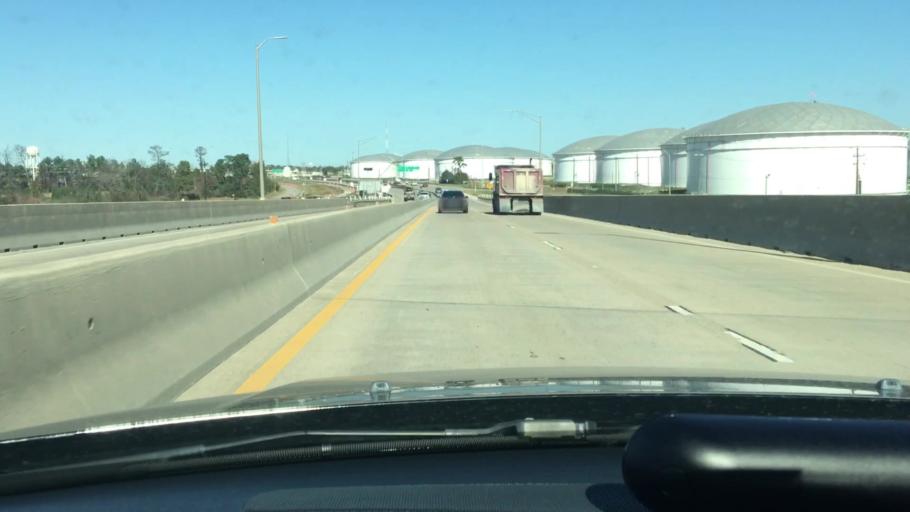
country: US
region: Texas
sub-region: Harris County
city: Cloverleaf
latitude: 29.7560
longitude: -95.1459
